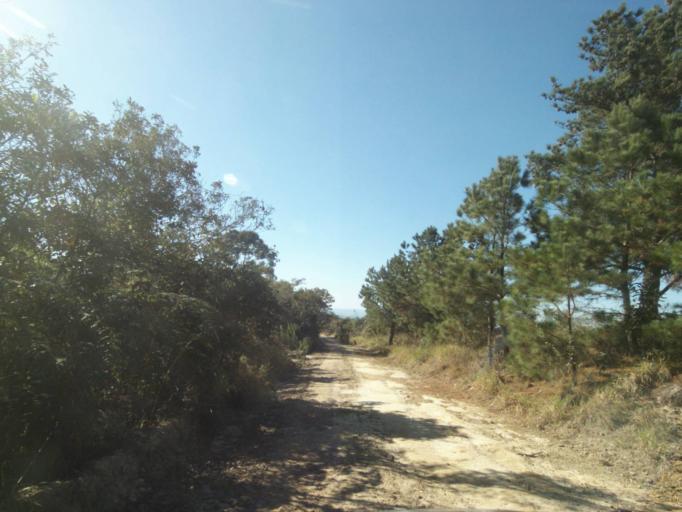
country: BR
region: Parana
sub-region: Tibagi
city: Tibagi
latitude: -24.5692
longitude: -50.4713
